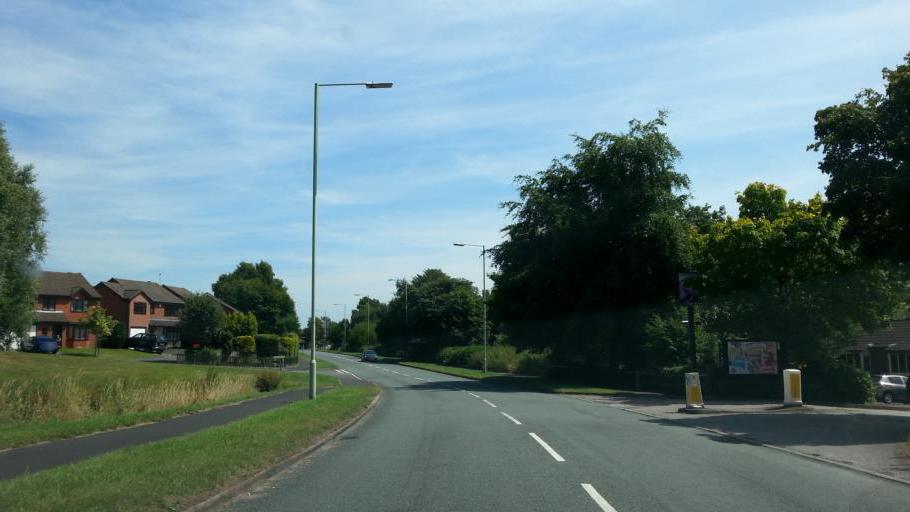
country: GB
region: England
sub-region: Staffordshire
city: Cannock
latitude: 52.7201
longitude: -2.0168
